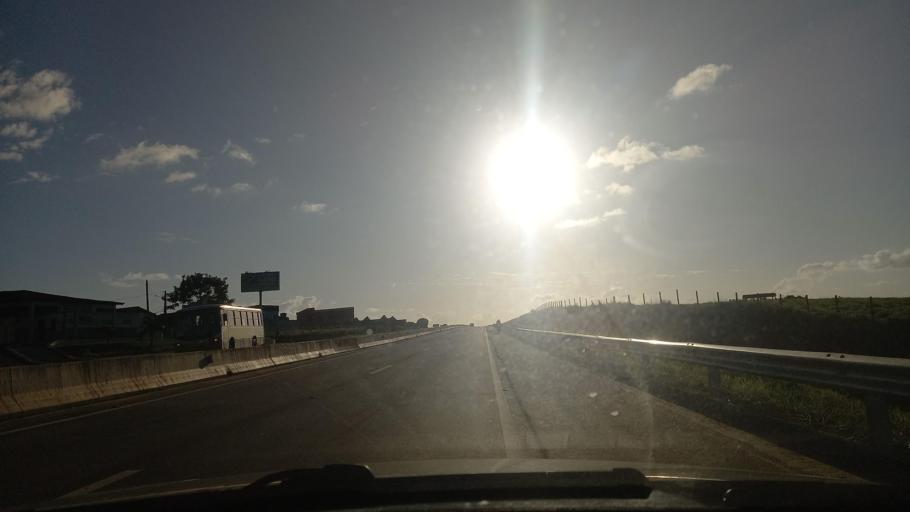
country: BR
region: Alagoas
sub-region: Campo Alegre
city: Campo Alegre
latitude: -9.8022
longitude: -36.2753
